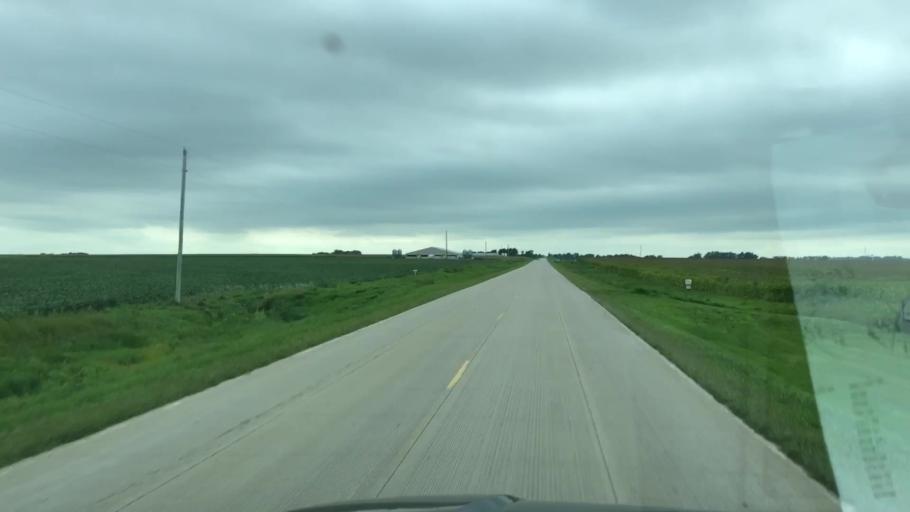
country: US
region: Iowa
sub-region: O'Brien County
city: Sheldon
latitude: 43.1318
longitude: -95.9792
